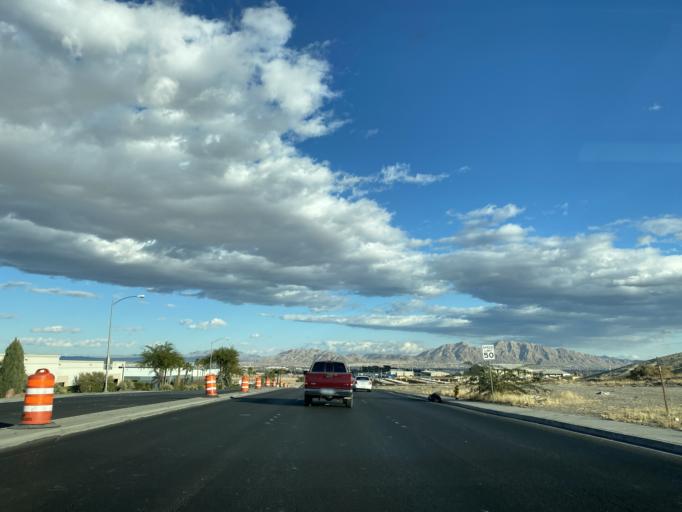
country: US
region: Nevada
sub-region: Clark County
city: North Las Vegas
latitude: 36.2178
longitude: -115.1518
